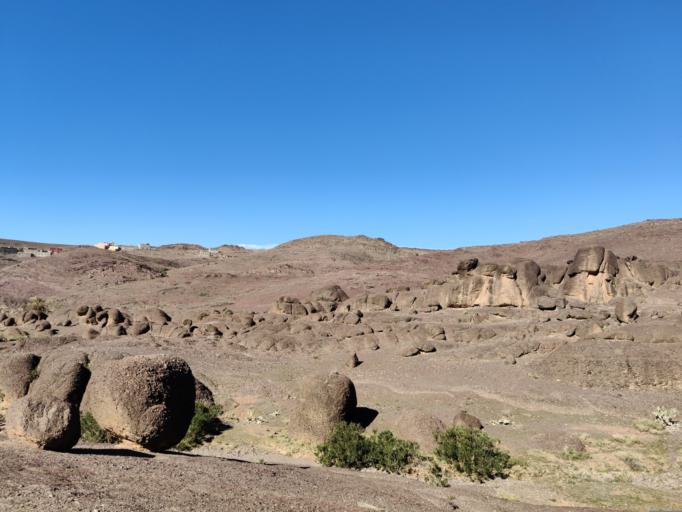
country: MA
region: Souss-Massa-Draa
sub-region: Taroudannt
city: Taliouine
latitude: 30.5558
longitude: -7.5936
